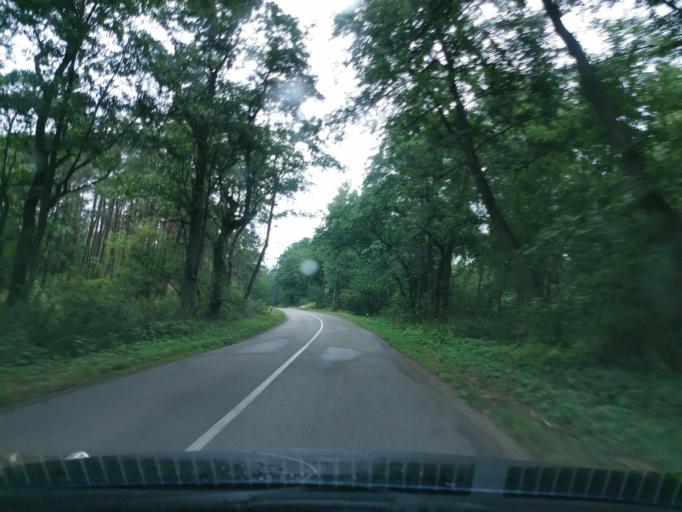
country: RU
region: Kaliningrad
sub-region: Zelenogradskiy Rayon
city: Zelenogradsk
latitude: 55.0899
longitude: 20.7328
